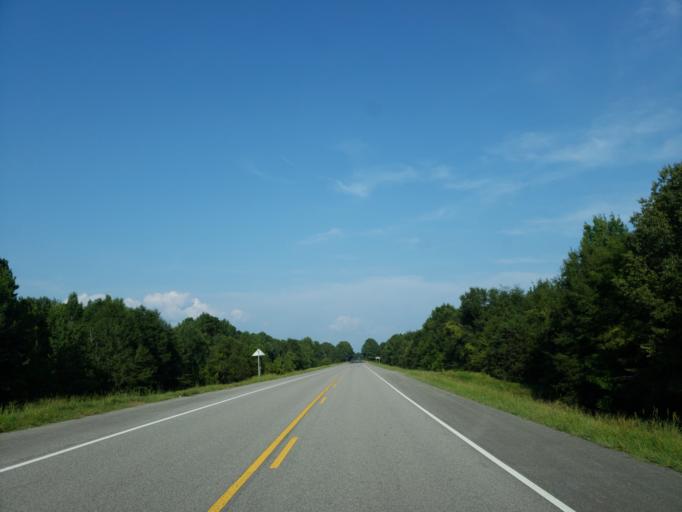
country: US
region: Alabama
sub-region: Sumter County
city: Livingston
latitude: 32.6974
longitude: -88.1077
